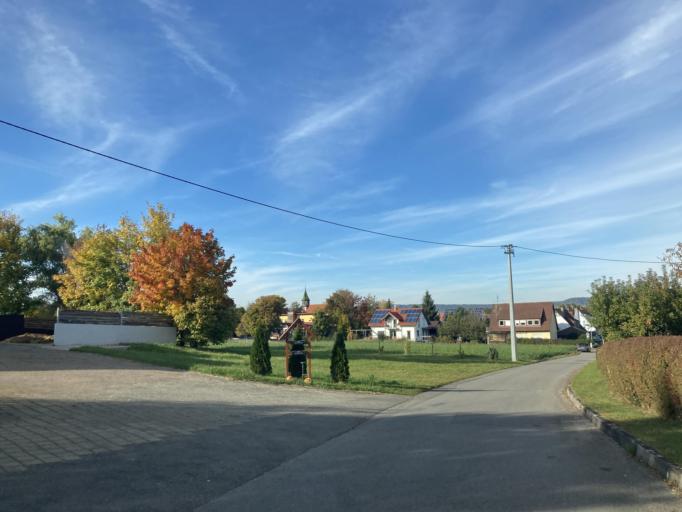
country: DE
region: Baden-Wuerttemberg
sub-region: Tuebingen Region
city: Rottenburg
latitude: 48.5231
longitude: 8.9635
